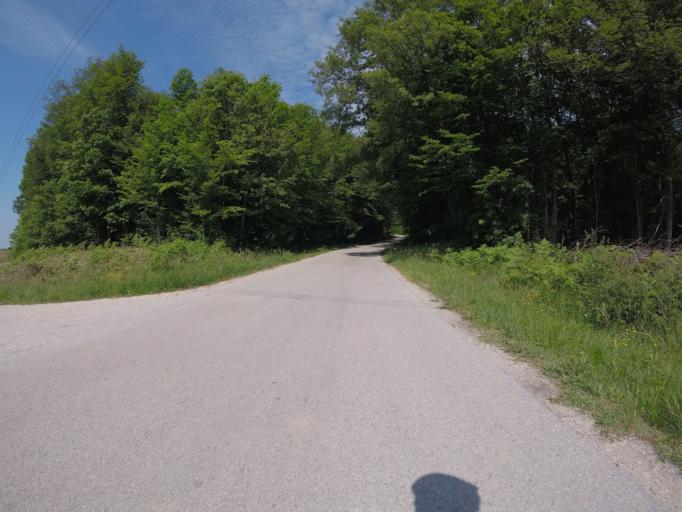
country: HR
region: Zagrebacka
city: Mraclin
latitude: 45.5728
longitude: 16.0138
